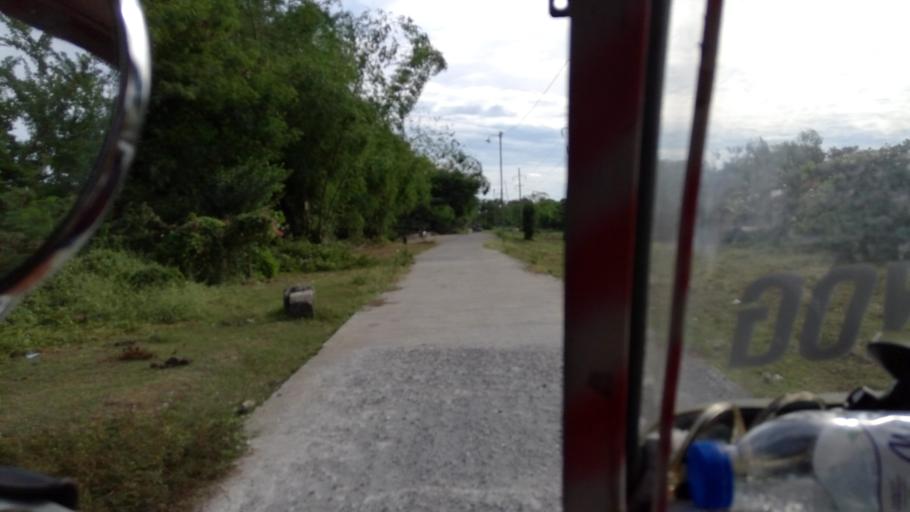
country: PH
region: Ilocos
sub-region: Province of La Union
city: San Eugenio
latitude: 16.3689
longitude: 120.3524
